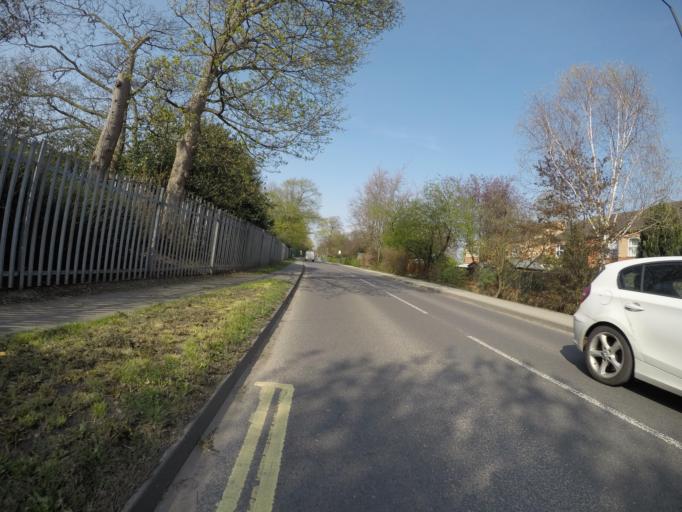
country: GB
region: England
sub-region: City of York
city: York
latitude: 53.9775
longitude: -1.0753
